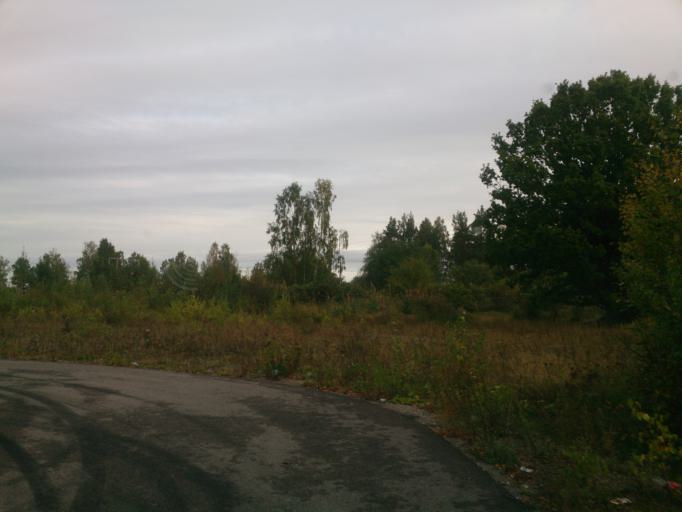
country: SE
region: OEstergoetland
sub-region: Atvidabergs Kommun
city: Atvidaberg
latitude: 58.2165
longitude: 15.9781
